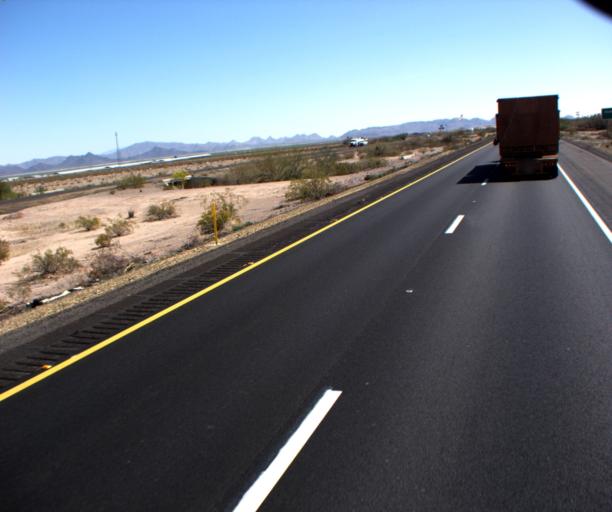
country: US
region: Arizona
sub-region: La Paz County
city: Salome
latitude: 33.6337
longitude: -113.7880
